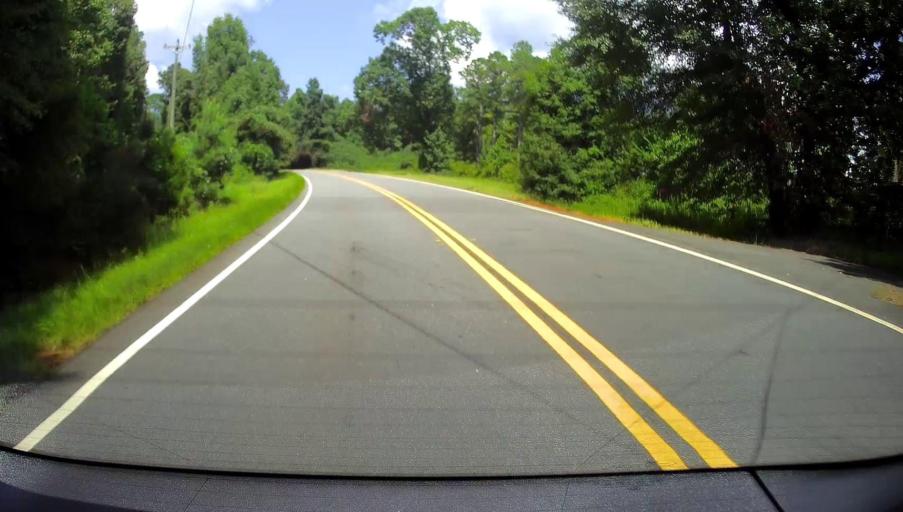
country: US
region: Georgia
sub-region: Crawford County
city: Knoxville
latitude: 32.8748
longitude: -83.9782
